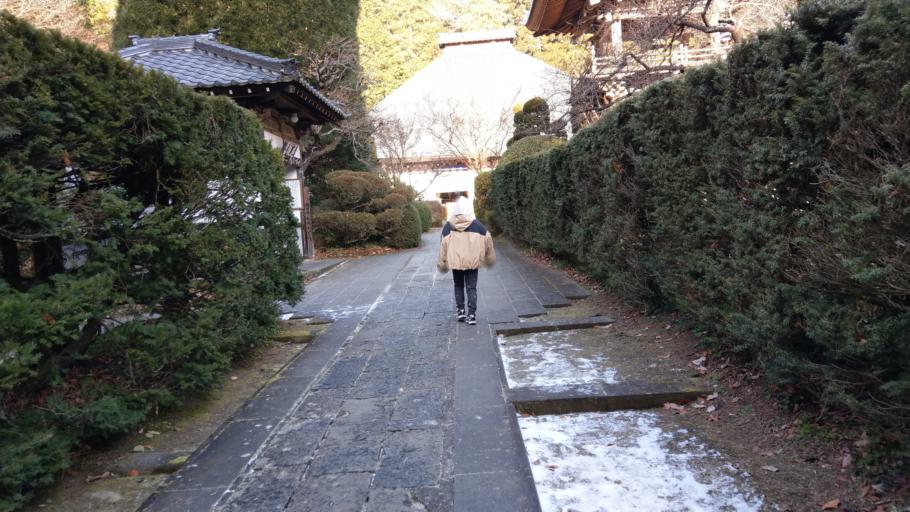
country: JP
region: Nagano
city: Kamimaruko
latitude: 36.3517
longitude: 138.1536
